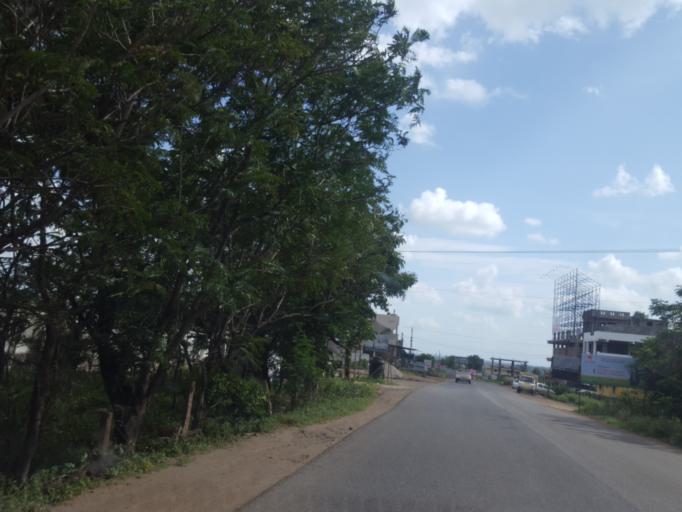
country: IN
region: Telangana
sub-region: Rangareddi
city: Singapur
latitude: 17.4546
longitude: 78.1451
